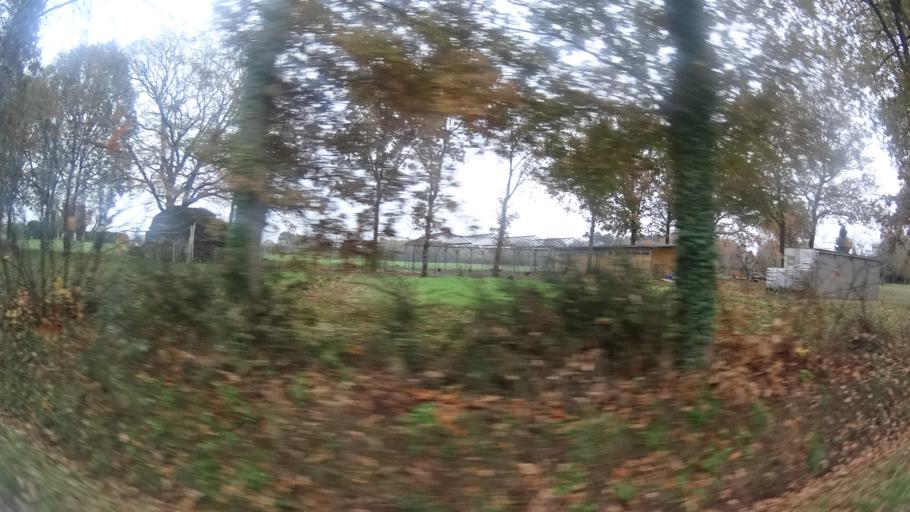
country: FR
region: Brittany
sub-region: Departement d'Ille-et-Vilaine
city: Sainte-Marie
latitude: 47.6971
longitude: -1.9982
